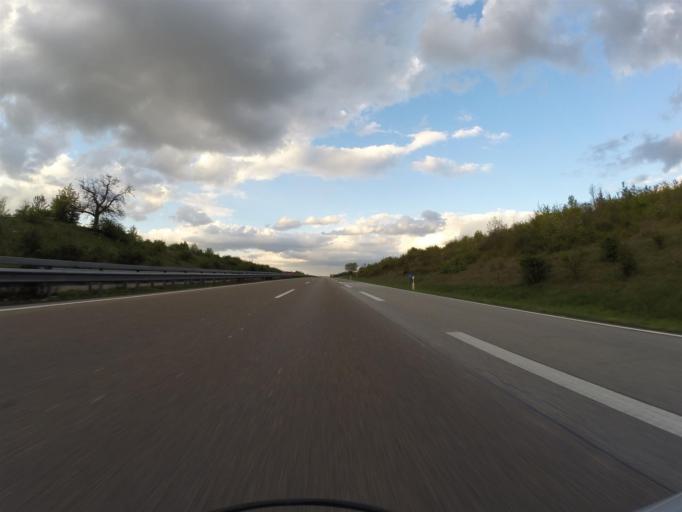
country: DE
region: Rheinland-Pfalz
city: Morschheim
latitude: 49.6852
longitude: 8.0350
